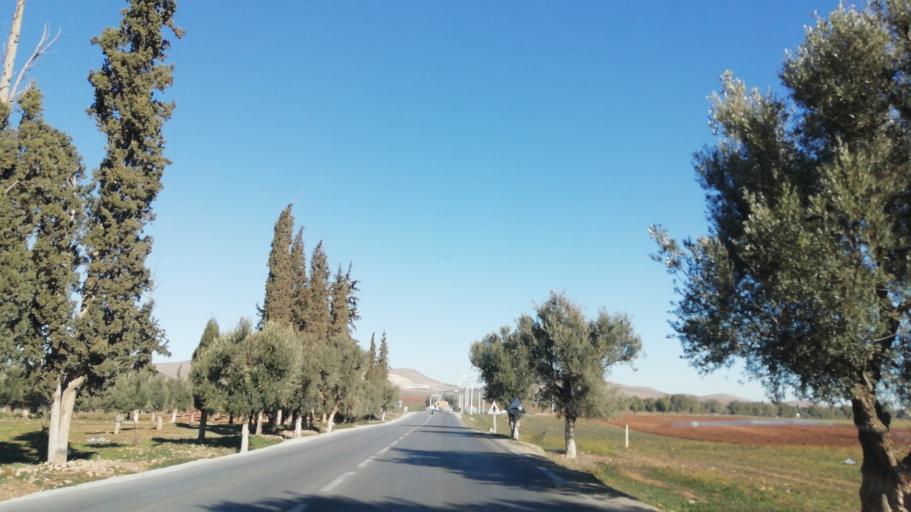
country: DZ
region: Mascara
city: Mascara
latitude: 35.2148
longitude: 0.1118
